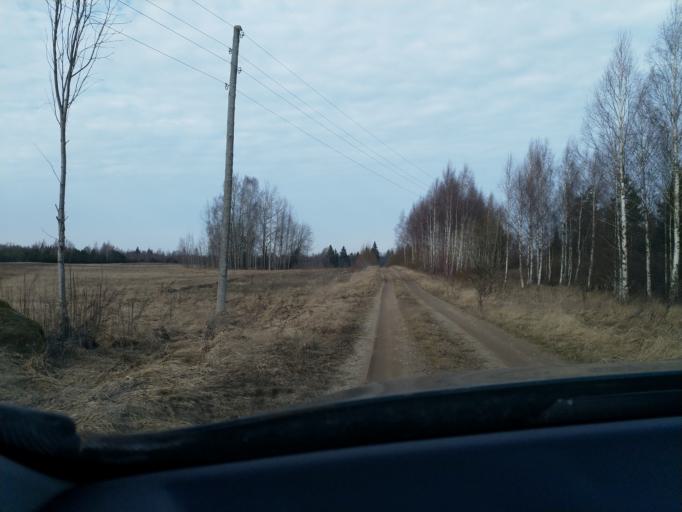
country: LV
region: Kuldigas Rajons
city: Kuldiga
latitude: 57.0429
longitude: 21.8551
